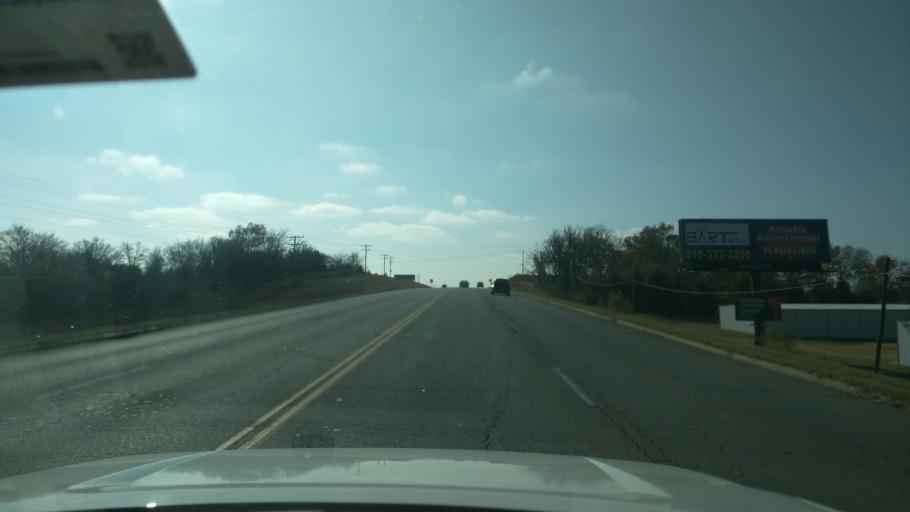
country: US
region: Oklahoma
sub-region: Washington County
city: Bartlesville
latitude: 36.6876
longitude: -95.9351
